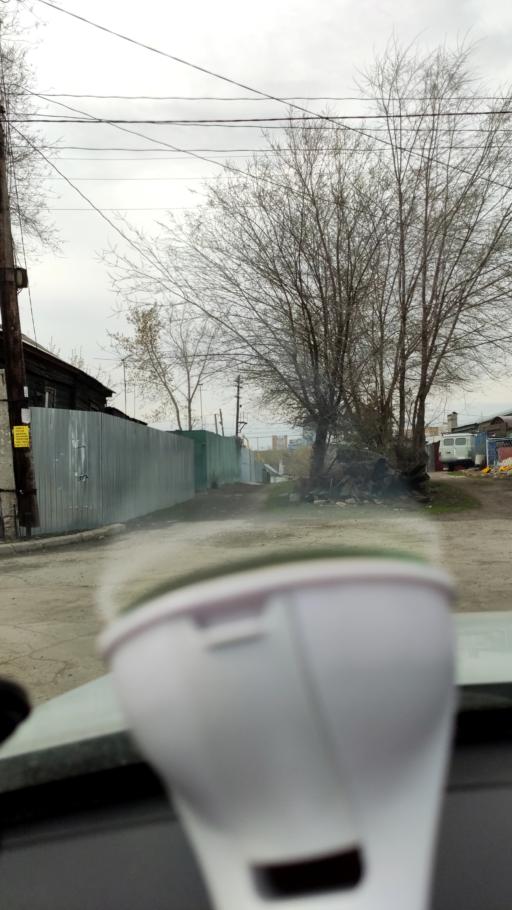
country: RU
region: Samara
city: Samara
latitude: 53.1809
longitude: 50.1334
